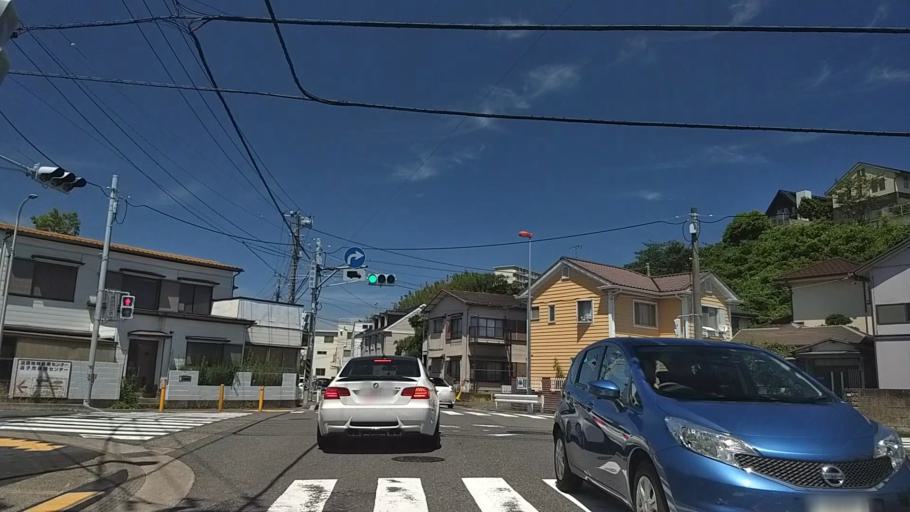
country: JP
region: Kanagawa
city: Zushi
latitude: 35.3025
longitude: 139.5914
